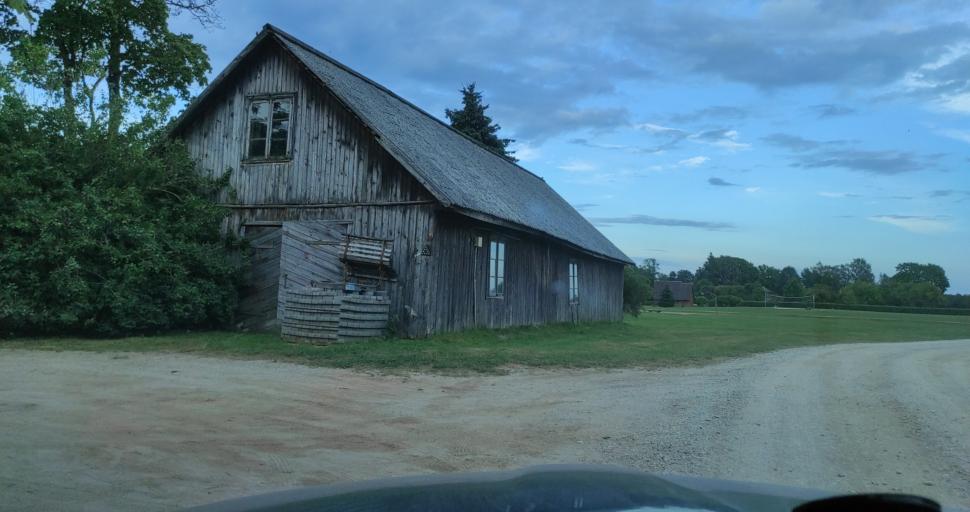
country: LV
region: Alsunga
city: Alsunga
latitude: 56.9344
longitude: 21.6408
